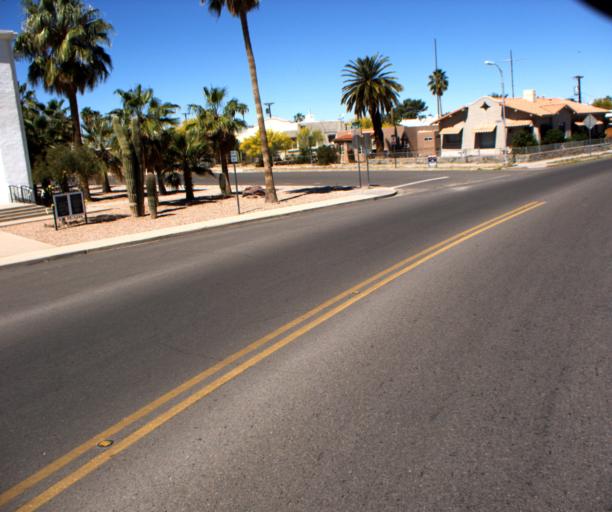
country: US
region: Arizona
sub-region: Pima County
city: Ajo
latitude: 32.3729
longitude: -112.8628
